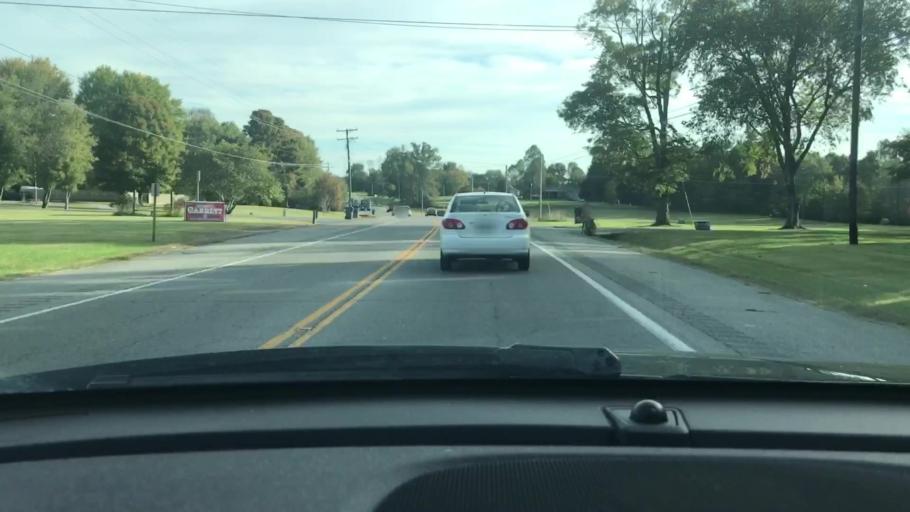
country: US
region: Tennessee
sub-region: Sumner County
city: Millersville
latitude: 36.4193
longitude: -86.6950
